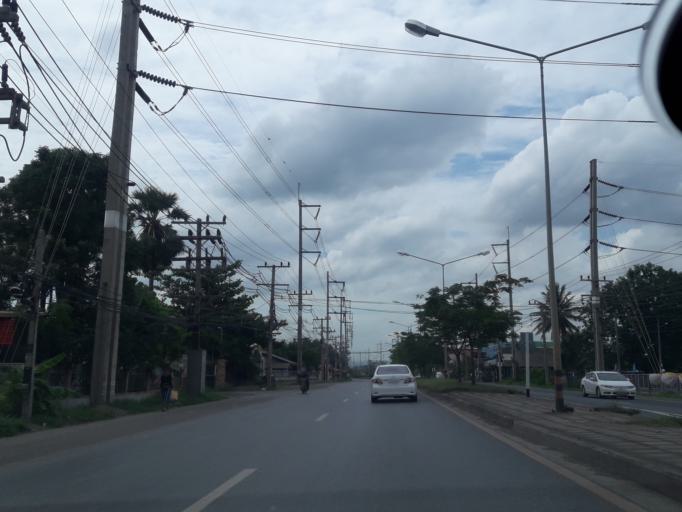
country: TH
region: Sara Buri
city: Kaeng Khoi
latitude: 14.5664
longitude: 101.0068
